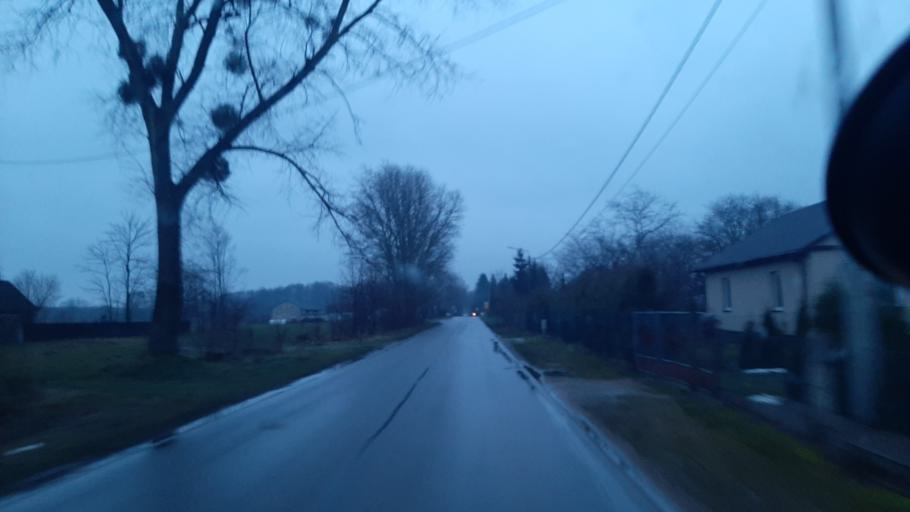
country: PL
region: Lublin Voivodeship
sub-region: Powiat lubelski
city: Garbow
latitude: 51.3914
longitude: 22.4112
